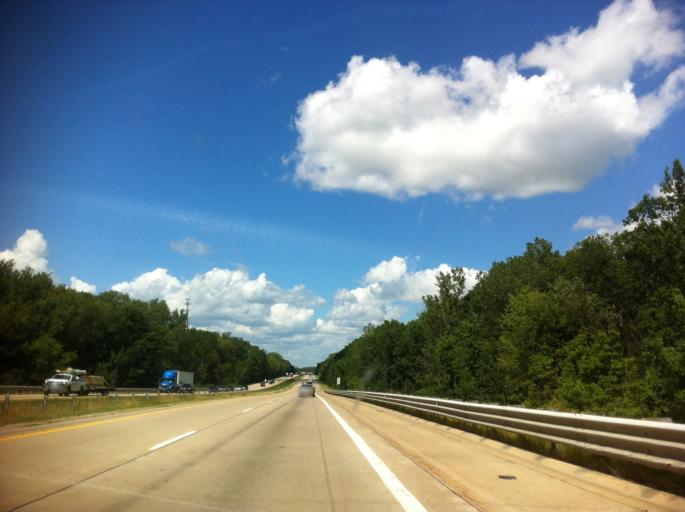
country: US
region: Michigan
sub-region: Monroe County
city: Dundee
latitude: 41.9156
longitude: -83.6619
